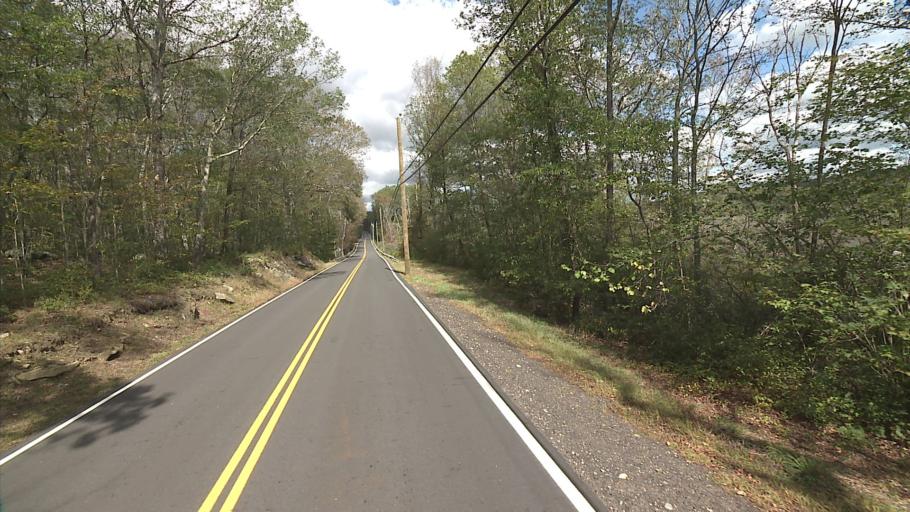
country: US
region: Connecticut
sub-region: Middlesex County
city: Higganum
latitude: 41.3991
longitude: -72.6045
